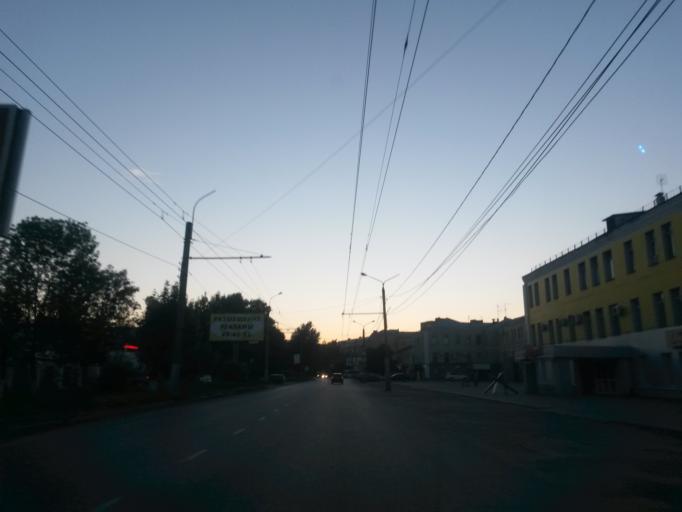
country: RU
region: Ivanovo
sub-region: Gorod Ivanovo
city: Ivanovo
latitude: 56.9965
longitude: 40.9602
